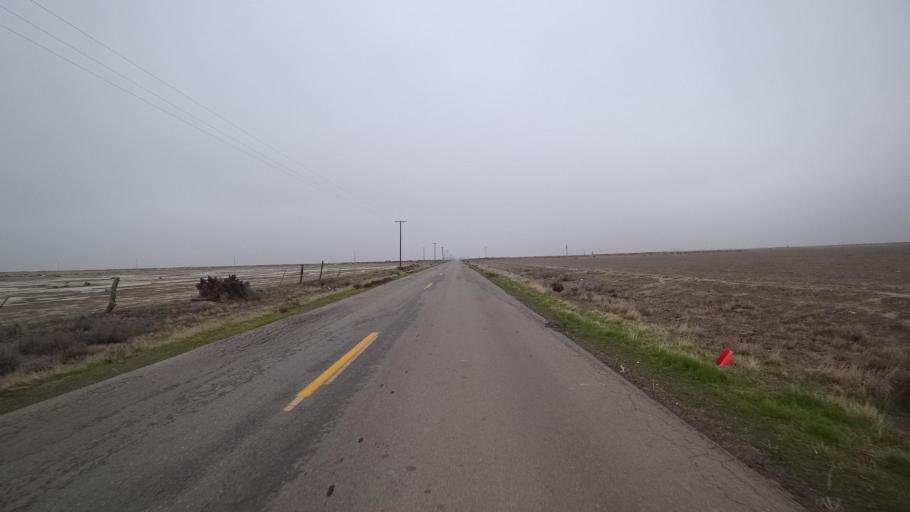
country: US
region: California
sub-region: Tulare County
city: Alpaugh
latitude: 35.7073
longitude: -119.4906
